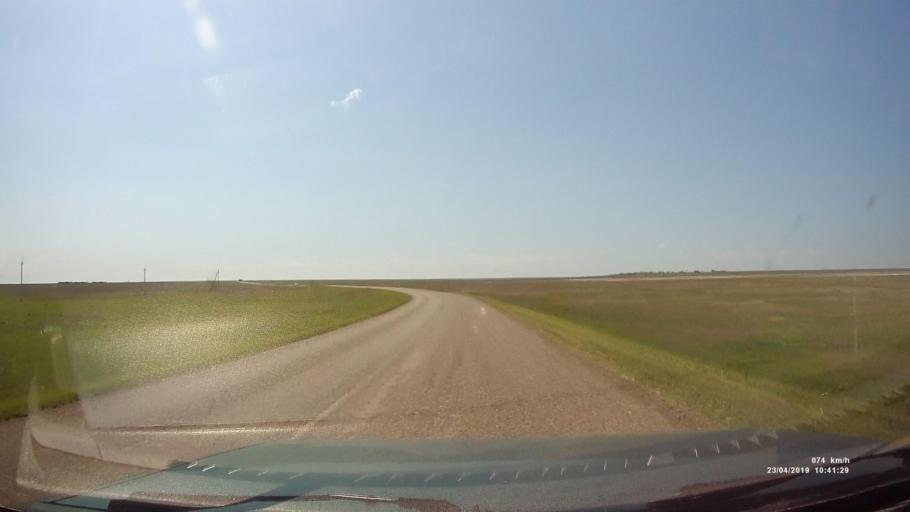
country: RU
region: Kalmykiya
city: Yashalta
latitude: 46.4934
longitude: 42.6378
